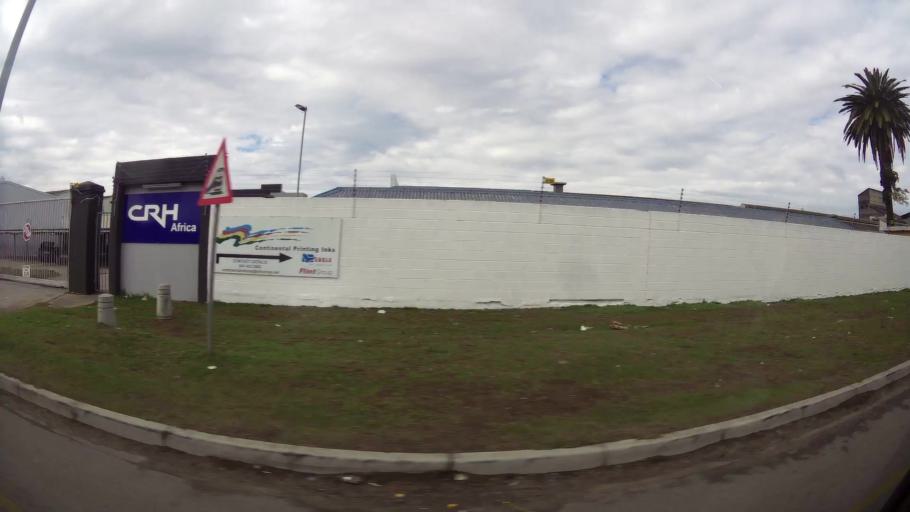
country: ZA
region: Eastern Cape
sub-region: Nelson Mandela Bay Metropolitan Municipality
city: Port Elizabeth
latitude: -33.9282
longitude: 25.5797
